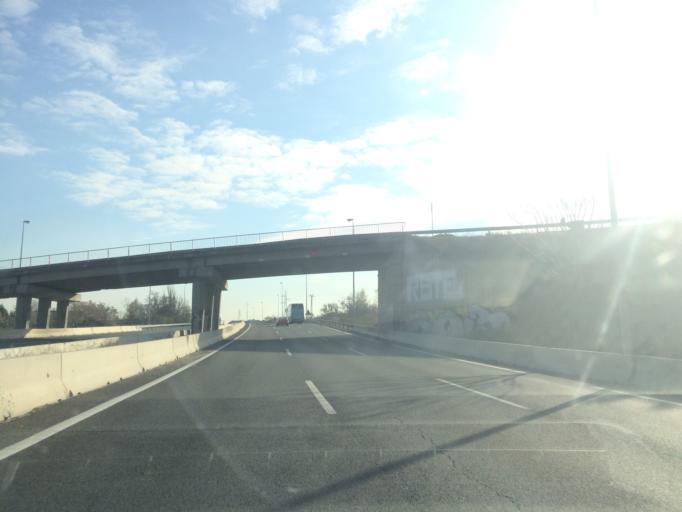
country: ES
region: Madrid
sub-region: Provincia de Madrid
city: Tres Cantos
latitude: 40.5495
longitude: -3.7053
